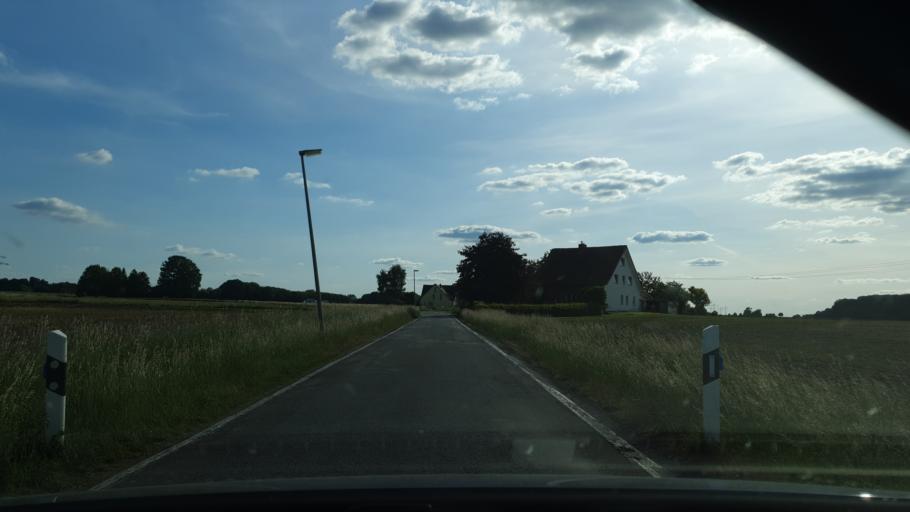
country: DE
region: North Rhine-Westphalia
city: Enger
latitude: 52.1649
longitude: 8.5395
